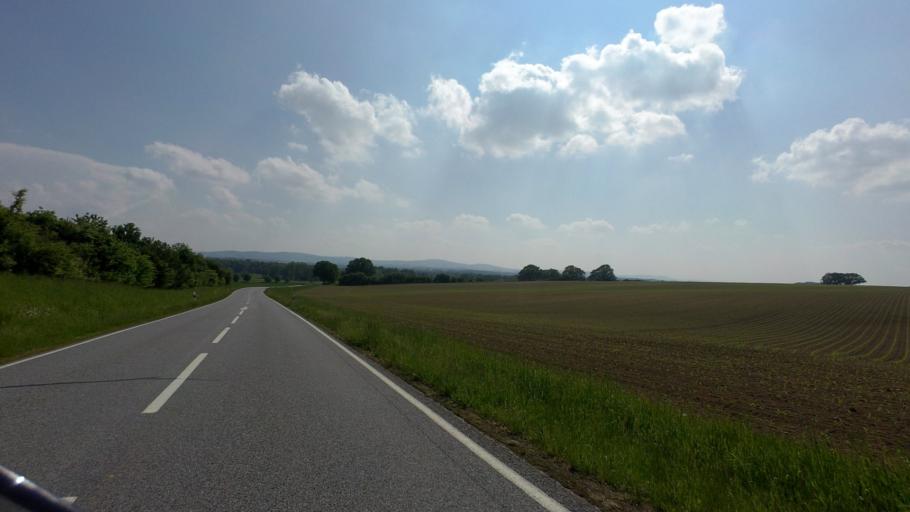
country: DE
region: Saxony
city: Weissenberg
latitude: 51.2060
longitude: 14.6056
